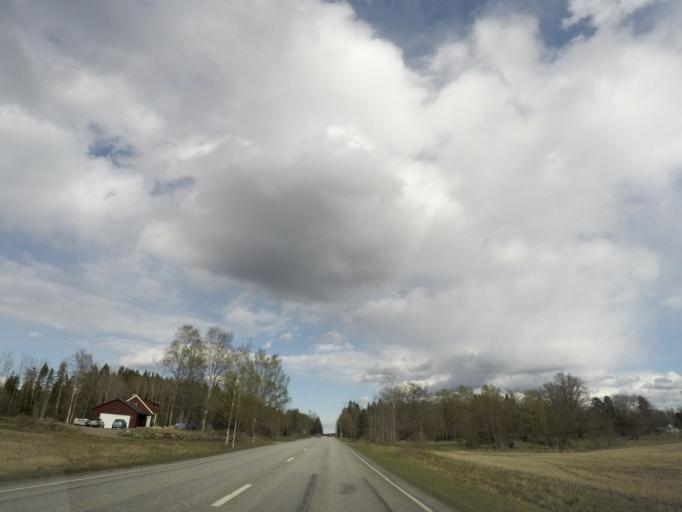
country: SE
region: Soedermanland
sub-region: Eskilstuna Kommun
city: Hallbybrunn
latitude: 59.3202
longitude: 16.3404
